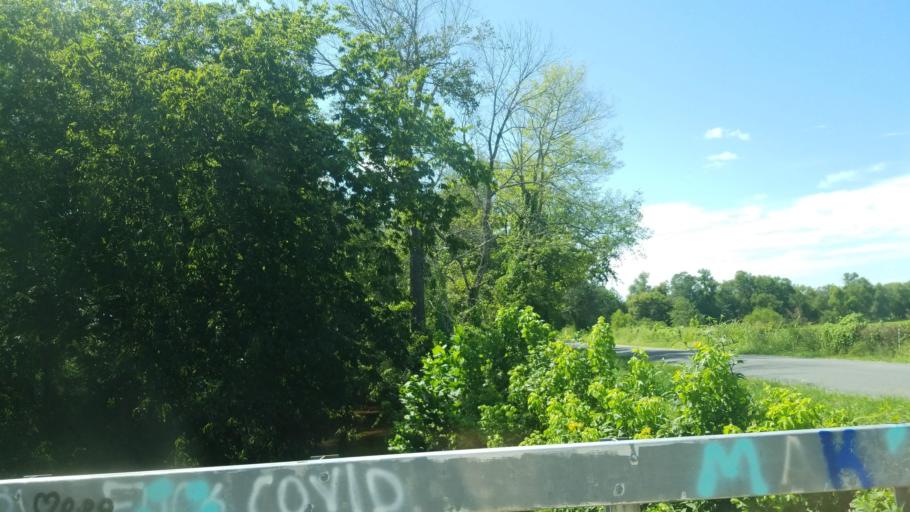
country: US
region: Illinois
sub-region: Williamson County
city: Johnston City
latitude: 37.7758
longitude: -88.8128
